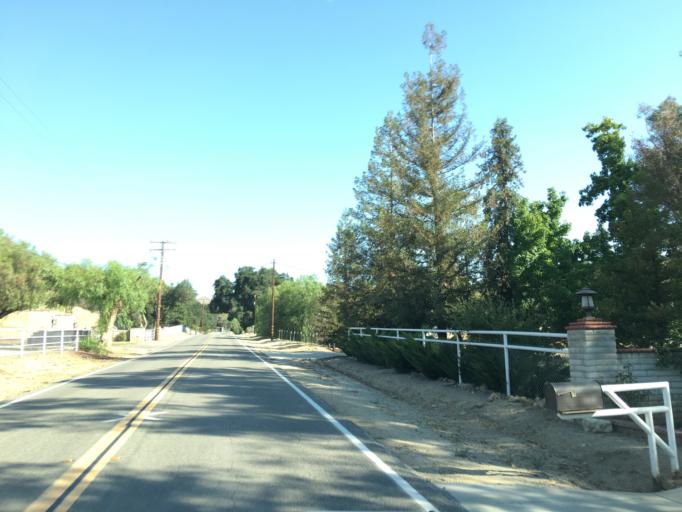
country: US
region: California
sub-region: Los Angeles County
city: Val Verde
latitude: 34.4692
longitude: -118.6684
